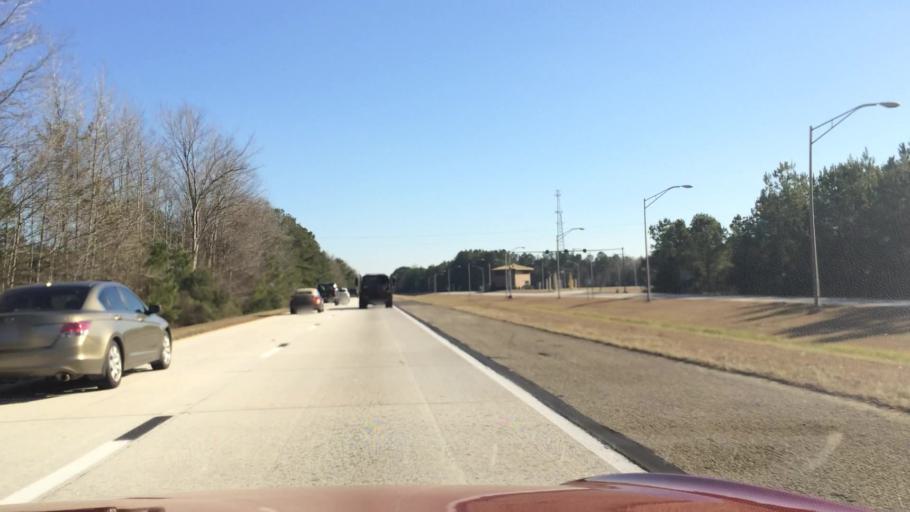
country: US
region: South Carolina
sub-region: Orangeburg County
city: Holly Hill
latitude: 33.2712
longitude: -80.4897
